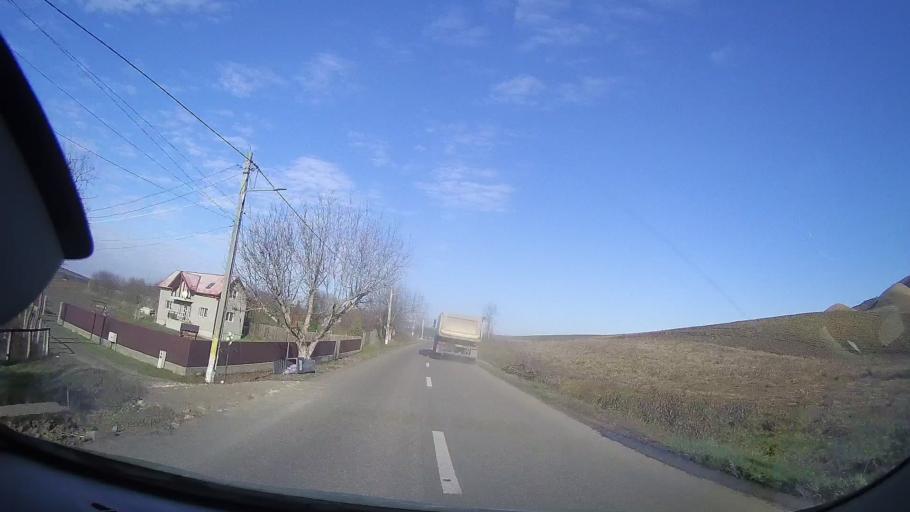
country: RO
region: Mures
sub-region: Comuna Iclanzel
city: Iclanzel
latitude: 46.5401
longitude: 24.3214
